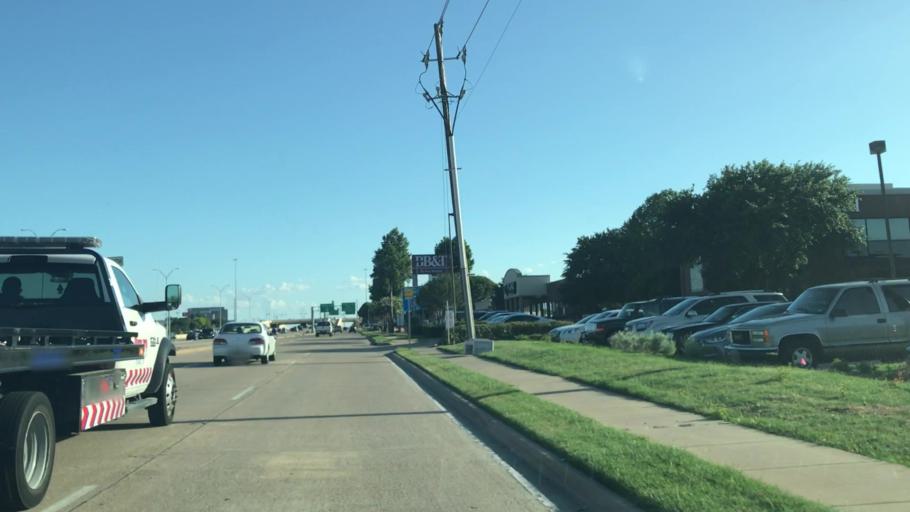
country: US
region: Texas
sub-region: Collin County
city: Plano
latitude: 33.0438
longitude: -96.7016
